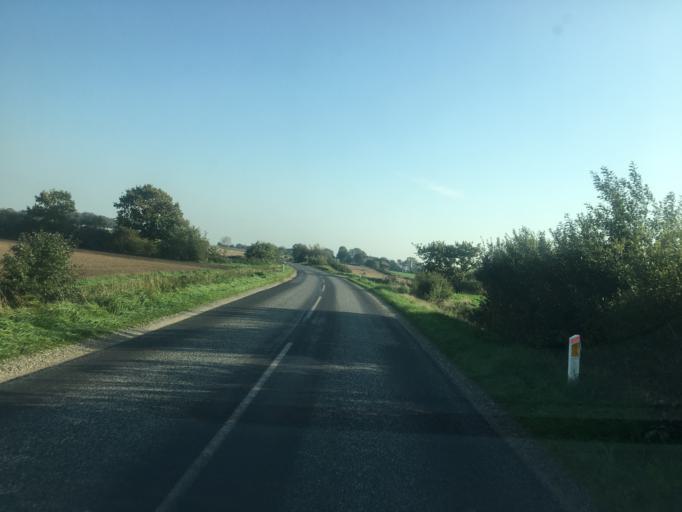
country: DE
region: Schleswig-Holstein
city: Bramstedtlund
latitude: 54.9553
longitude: 9.0540
